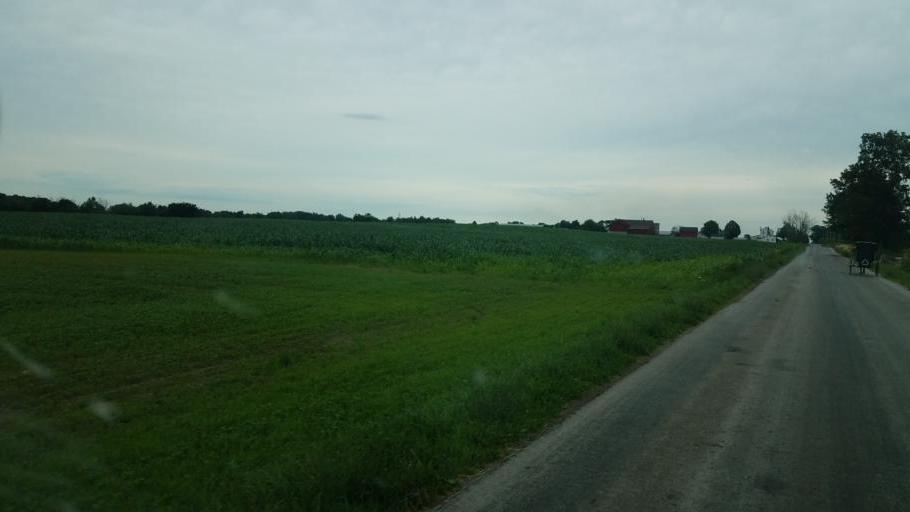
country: US
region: Ohio
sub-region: Ashland County
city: Ashland
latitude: 40.9314
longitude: -82.4204
